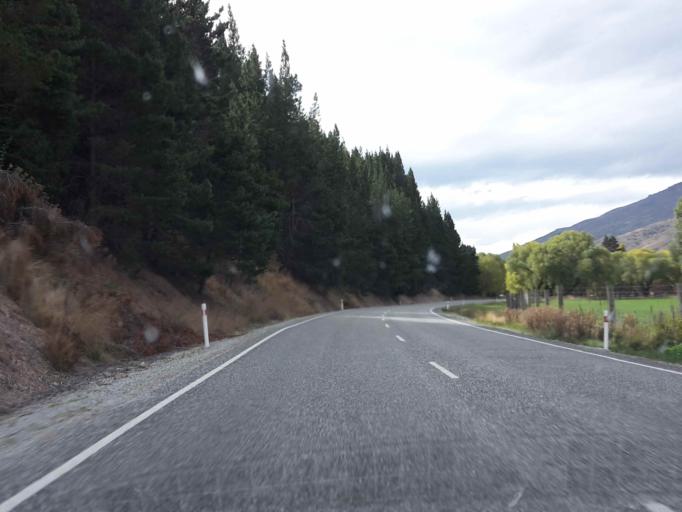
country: NZ
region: Otago
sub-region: Queenstown-Lakes District
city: Wanaka
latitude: -44.8382
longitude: 169.0530
